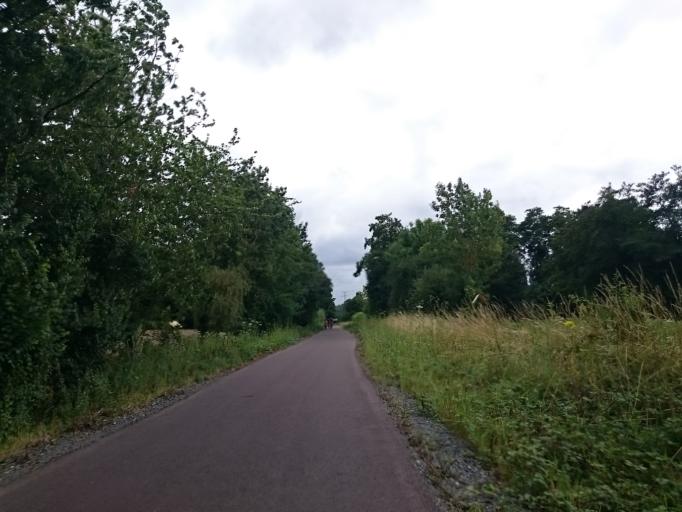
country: FR
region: Lower Normandy
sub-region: Departement du Calvados
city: Louvigny
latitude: 49.1370
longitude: -0.3961
